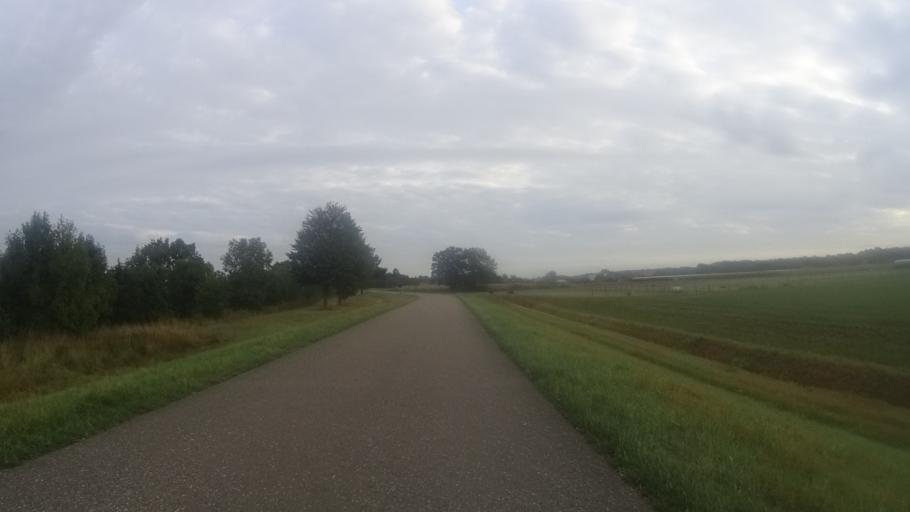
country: NL
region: Limburg
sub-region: Gemeente Venlo
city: Venlo
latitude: 51.4214
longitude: 6.1596
